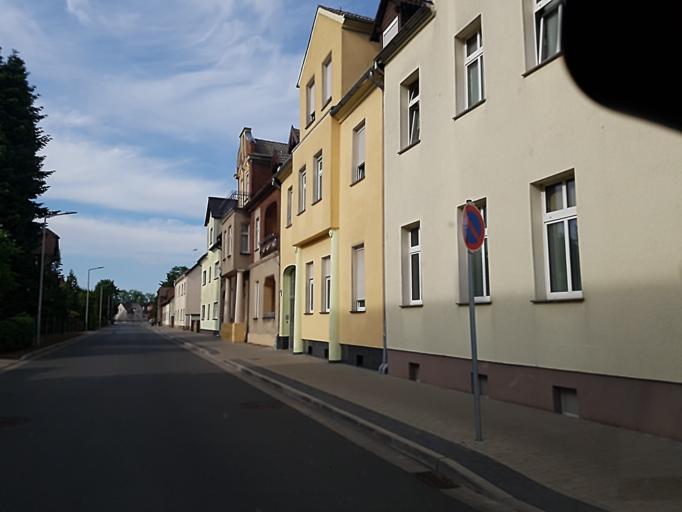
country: DE
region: Saxony-Anhalt
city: Jessen
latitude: 51.7904
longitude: 12.9619
